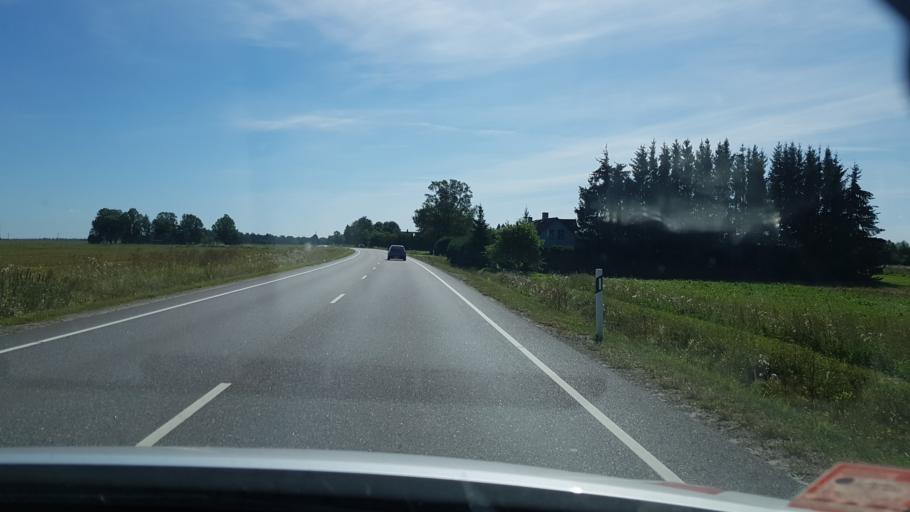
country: EE
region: Tartu
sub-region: Tartu linn
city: Tartu
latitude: 58.4216
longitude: 26.8647
